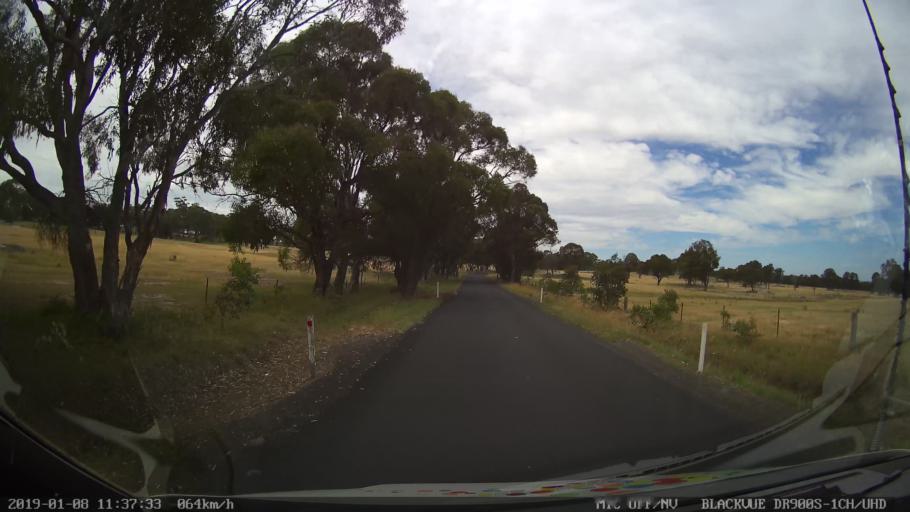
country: AU
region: New South Wales
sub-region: Guyra
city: Guyra
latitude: -30.3529
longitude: 151.5522
